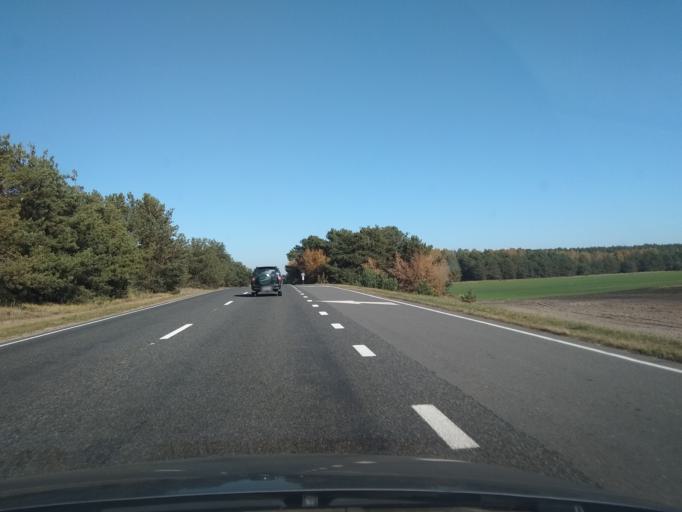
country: BY
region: Brest
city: Kobryn
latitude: 52.1316
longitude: 24.3059
